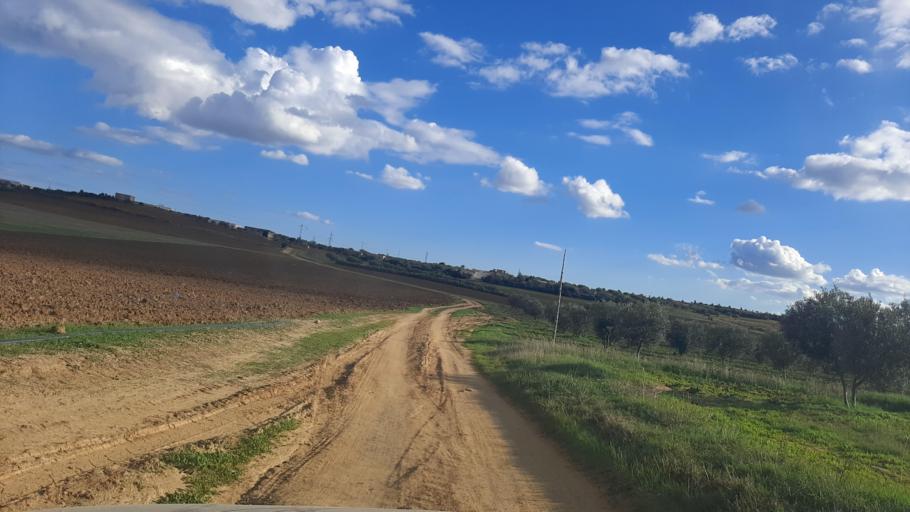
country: TN
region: Nabul
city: Bu `Urqub
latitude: 36.4463
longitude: 10.5022
